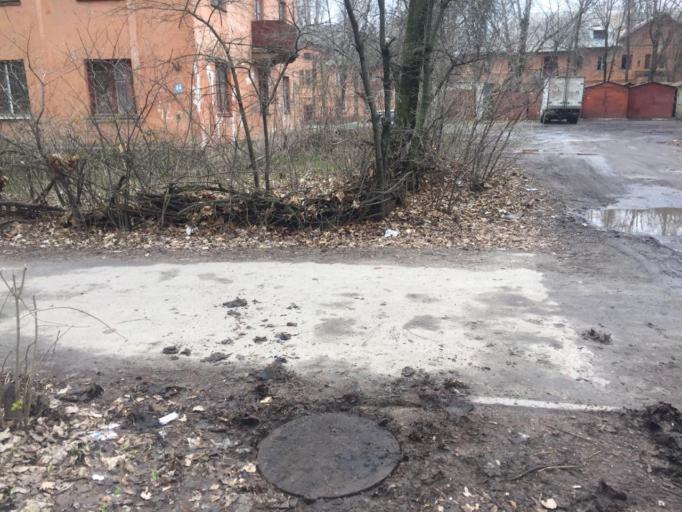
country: RU
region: Voronezj
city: Voronezh
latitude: 51.6784
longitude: 39.1544
